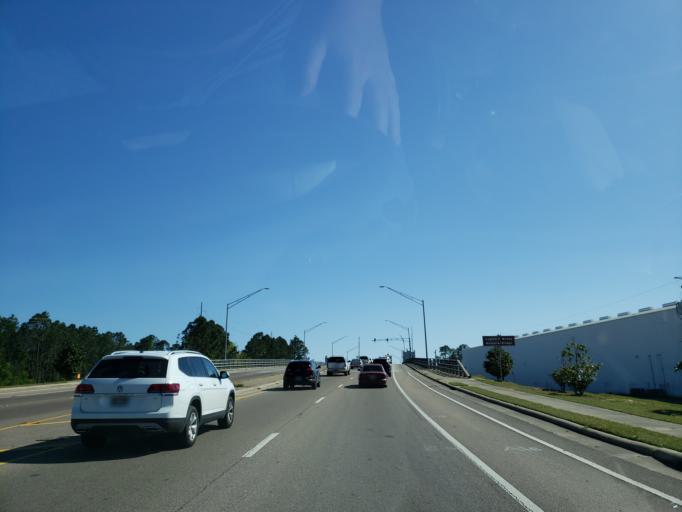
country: US
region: Mississippi
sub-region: Harrison County
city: West Gulfport
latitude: 30.4272
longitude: -89.0315
